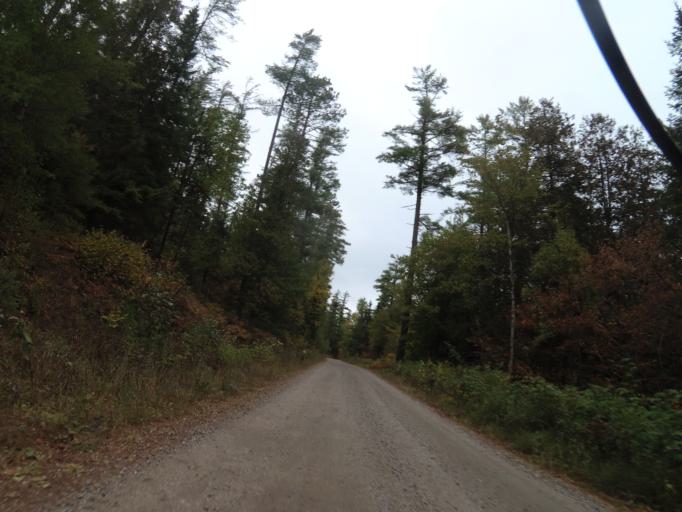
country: CA
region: Ontario
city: Renfrew
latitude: 45.2500
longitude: -77.0233
